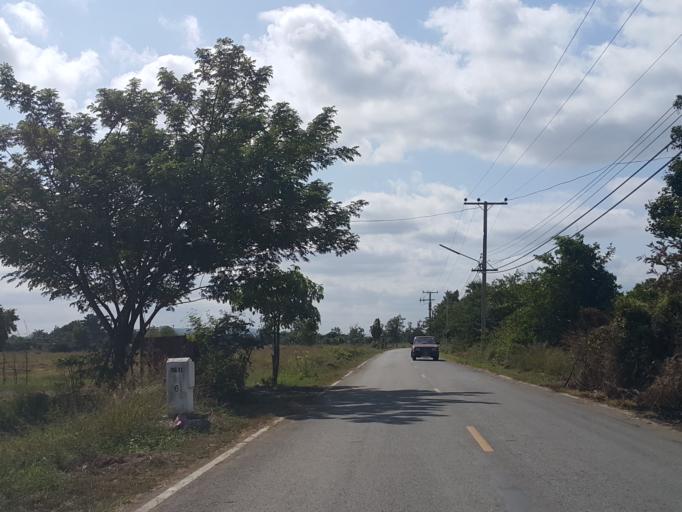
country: TH
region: Lamphun
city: Ban Thi
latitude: 18.5734
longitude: 99.0873
